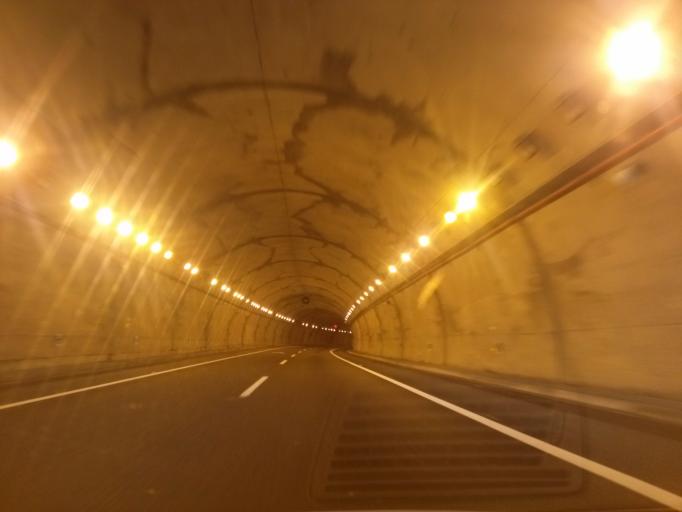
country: ES
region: Galicia
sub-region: Provincia de Lugo
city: Becerrea
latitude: 42.7845
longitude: -7.1056
